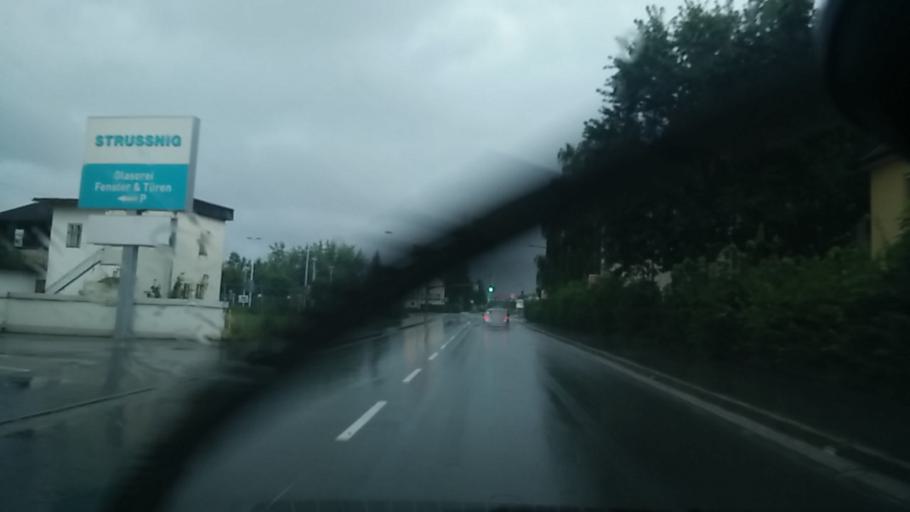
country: AT
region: Carinthia
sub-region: Villach Stadt
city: Villach
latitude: 46.5979
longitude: 13.8386
